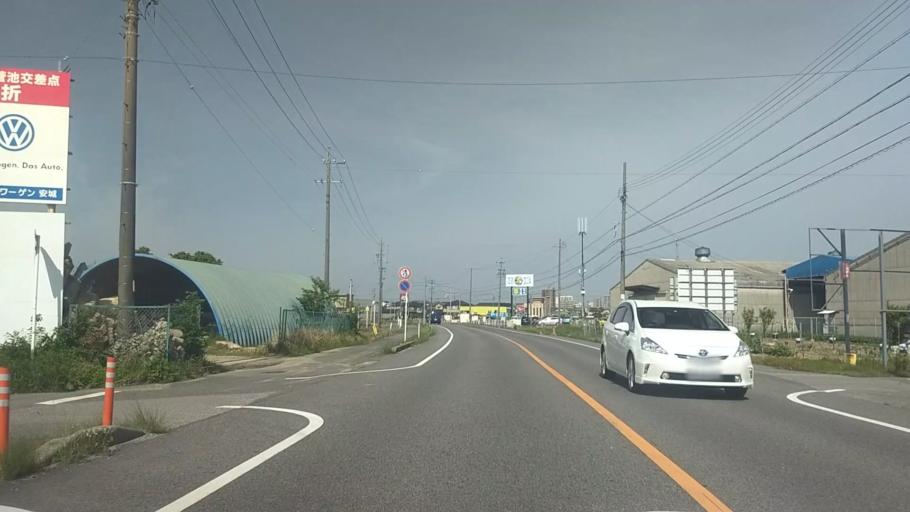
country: JP
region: Aichi
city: Anjo
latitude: 34.9494
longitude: 137.1046
